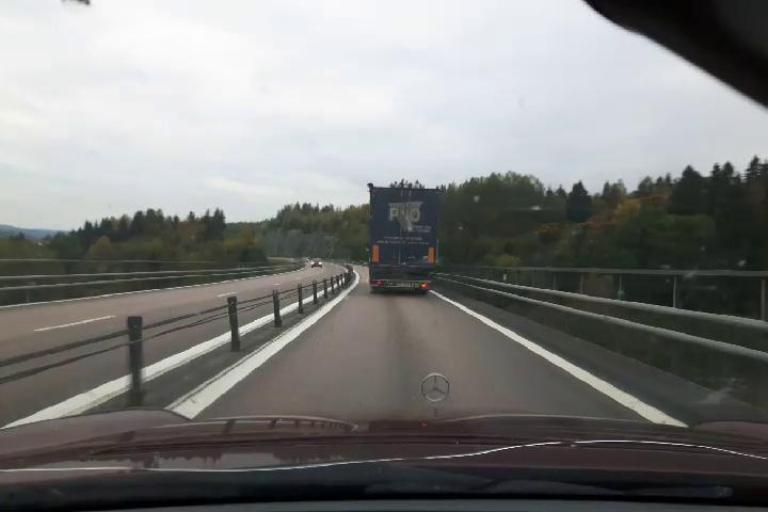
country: SE
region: Vaesternorrland
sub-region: Haernoesands Kommun
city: Haernoesand
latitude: 62.8317
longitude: 17.9676
